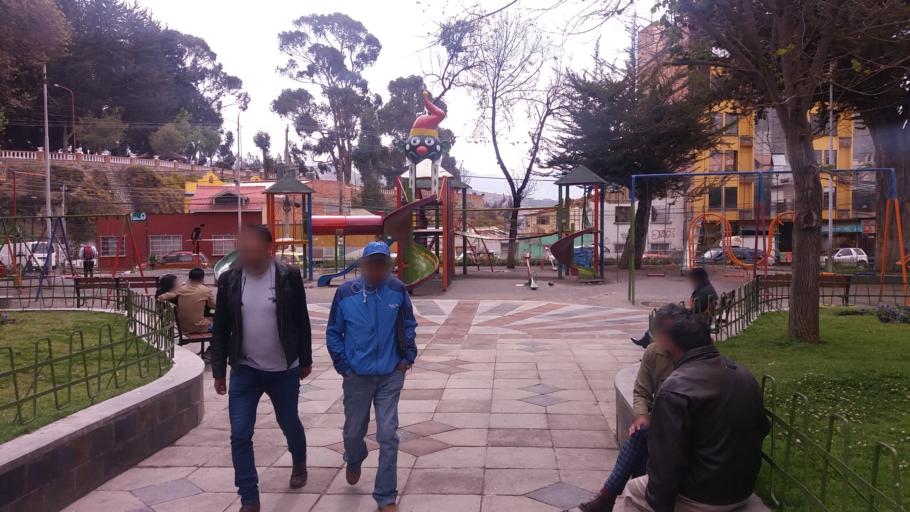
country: BO
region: La Paz
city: La Paz
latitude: -16.5144
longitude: -68.1284
